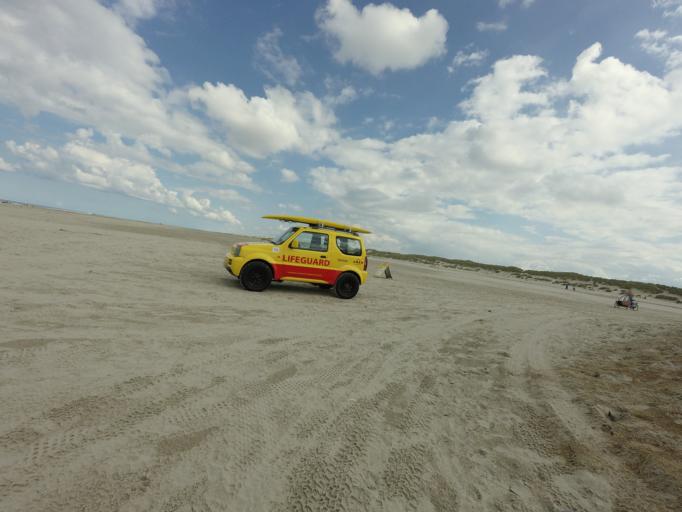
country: NL
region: Friesland
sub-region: Gemeente Terschelling
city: West-Terschelling
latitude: 53.4035
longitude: 5.2509
